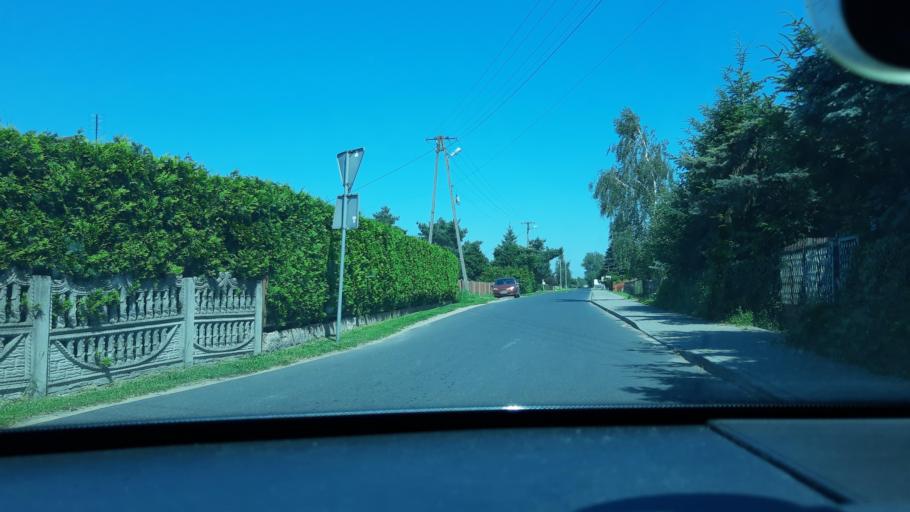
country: PL
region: Lodz Voivodeship
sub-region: Powiat zdunskowolski
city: Zdunska Wola
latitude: 51.6225
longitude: 18.9656
